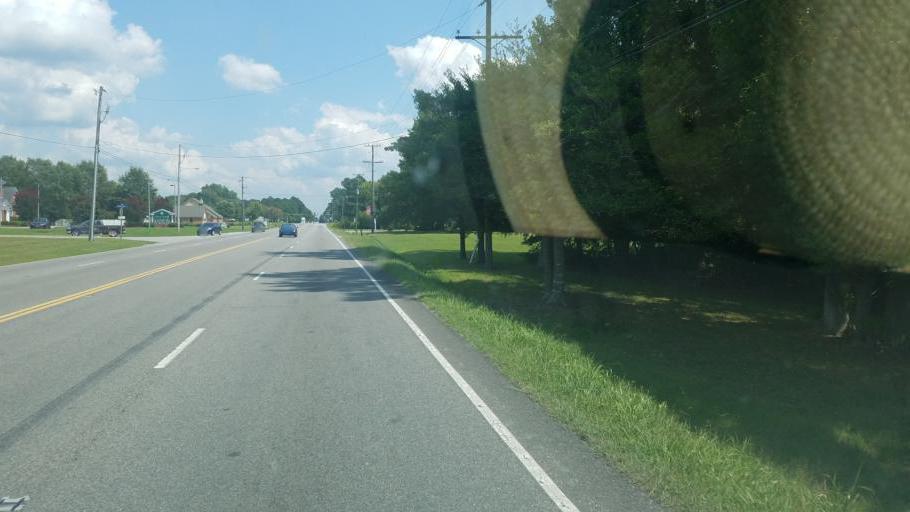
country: US
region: Virginia
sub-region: Isle of Wight County
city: Windsor
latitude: 36.8050
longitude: -76.7317
